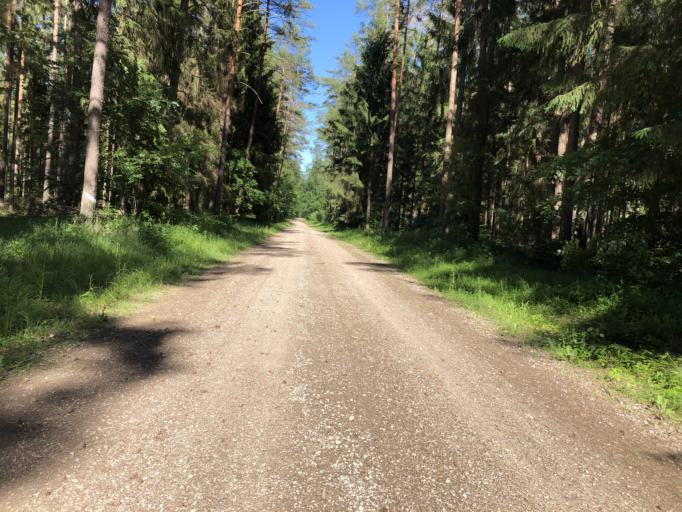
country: DE
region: Bavaria
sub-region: Upper Franconia
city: Memmelsdorf
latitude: 49.9117
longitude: 10.9629
